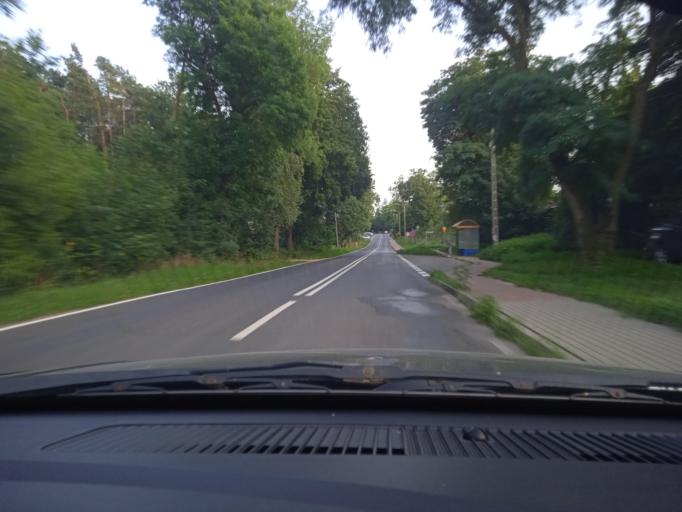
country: PL
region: Masovian Voivodeship
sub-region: Powiat nowodworski
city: Pomiechowek
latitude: 52.4772
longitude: 20.7248
